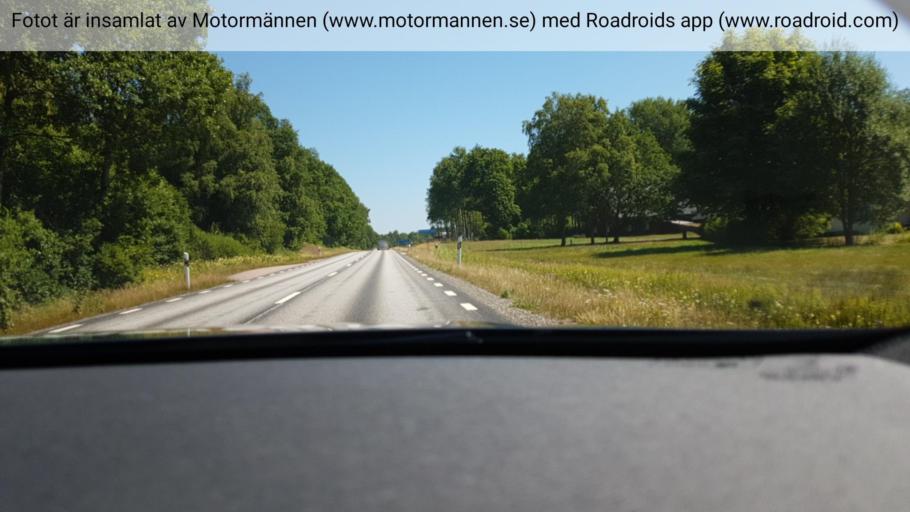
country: SE
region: Joenkoeping
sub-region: Gnosjo Kommun
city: Hillerstorp
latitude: 57.3210
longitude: 13.8654
